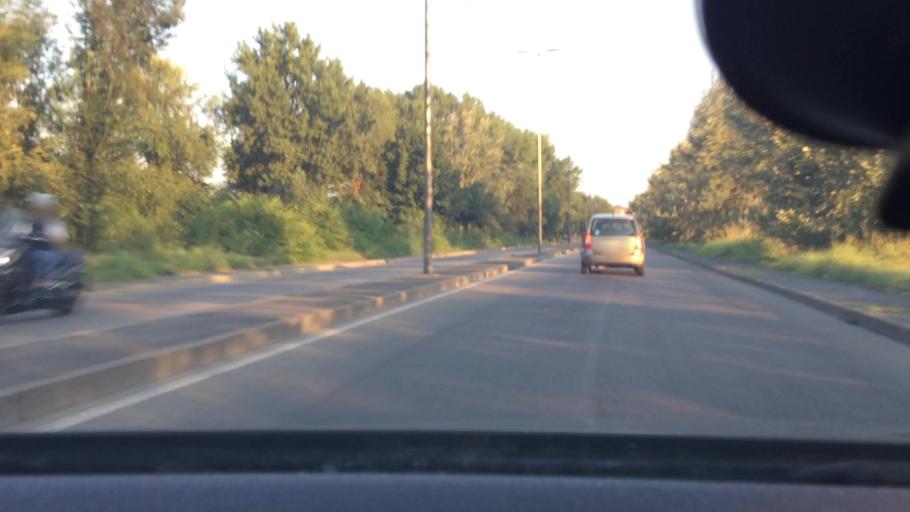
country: IT
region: Lombardy
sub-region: Citta metropolitana di Milano
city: Figino
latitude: 45.5010
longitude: 9.0736
